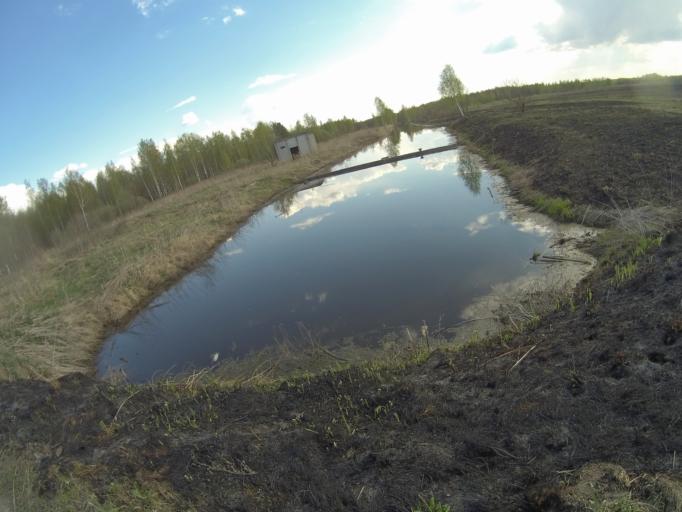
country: RU
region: Vladimir
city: Orgtrud
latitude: 56.2455
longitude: 40.7402
